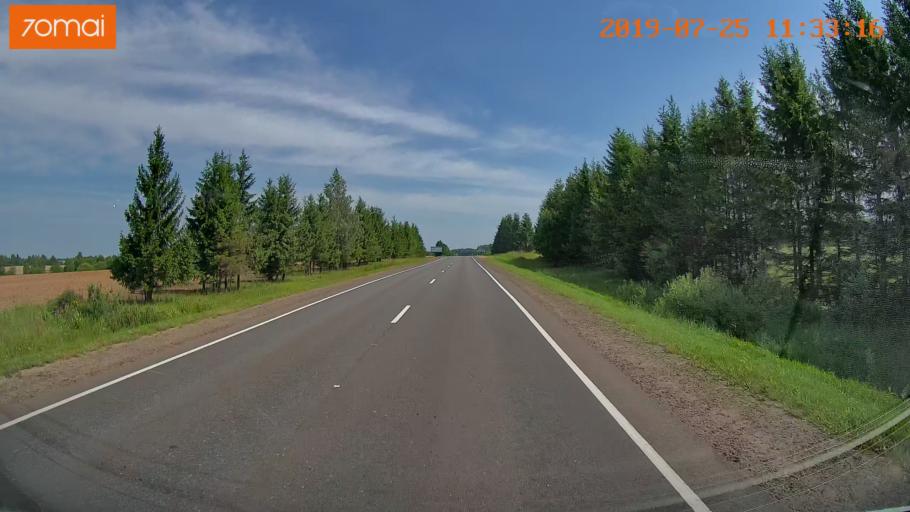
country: RU
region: Ivanovo
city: Privolzhsk
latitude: 57.3928
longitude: 41.3869
